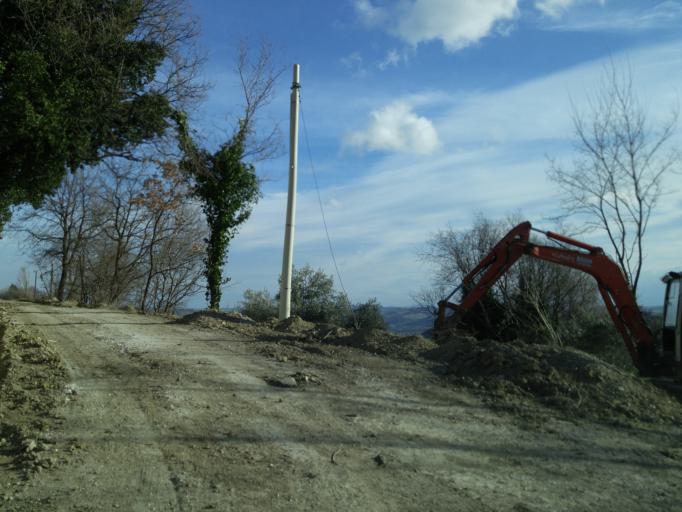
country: IT
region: The Marches
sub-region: Provincia di Pesaro e Urbino
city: Cartoceto
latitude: 43.7614
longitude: 12.8761
